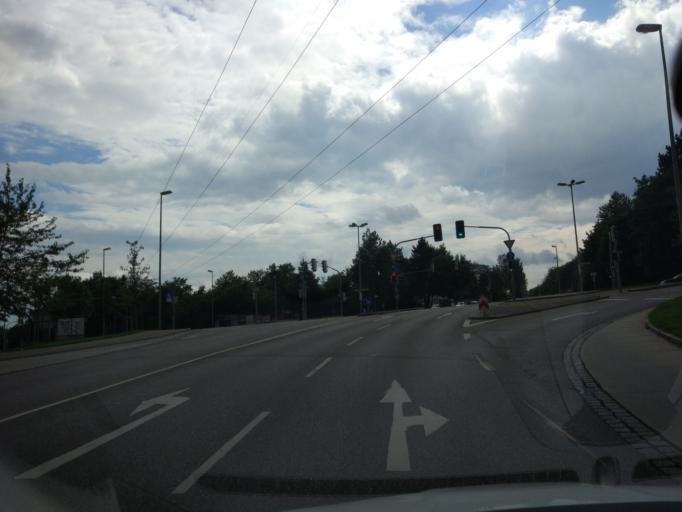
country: DE
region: Bavaria
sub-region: Swabia
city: Neu-Ulm
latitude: 48.4259
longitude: 10.0122
